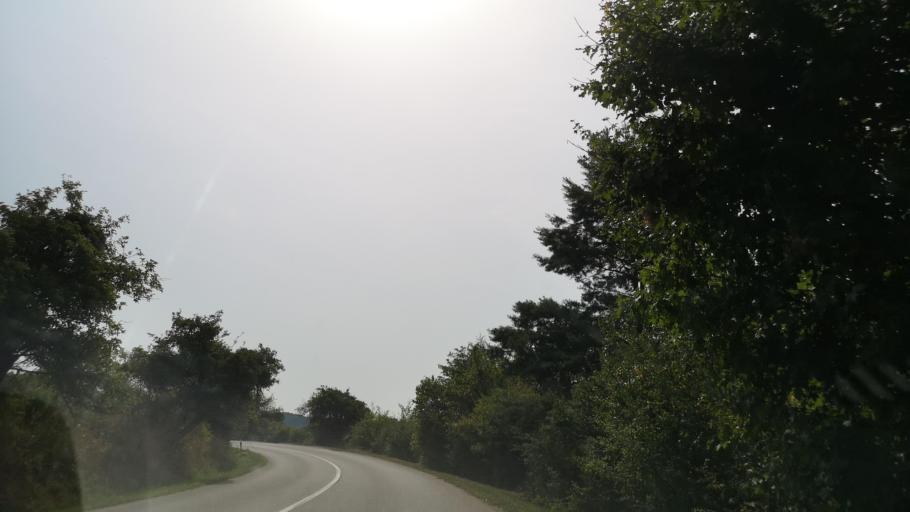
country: SK
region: Banskobystricky
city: Revuca
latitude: 48.6036
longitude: 20.1591
